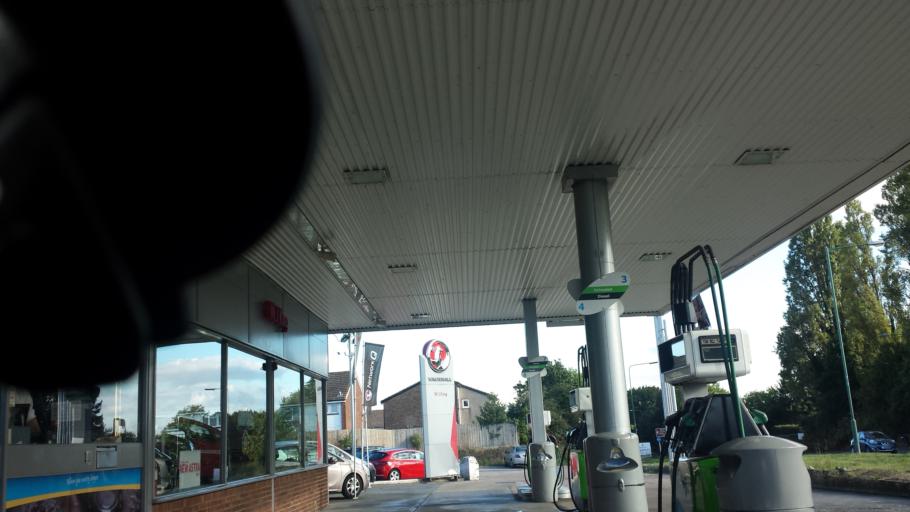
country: GB
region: England
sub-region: Kent
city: Swanley
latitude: 51.4051
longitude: 0.1592
